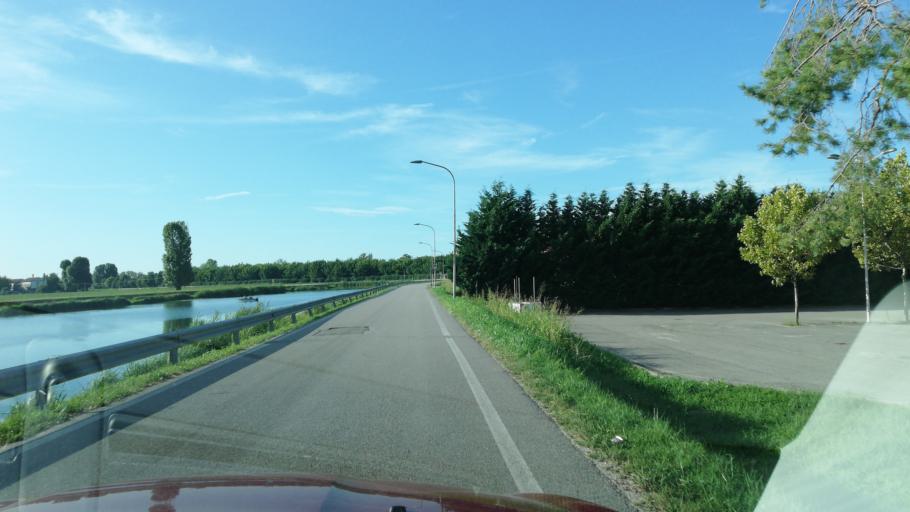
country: IT
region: Veneto
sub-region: Provincia di Venezia
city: San Giorgio di Livenza
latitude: 45.6435
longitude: 12.7901
